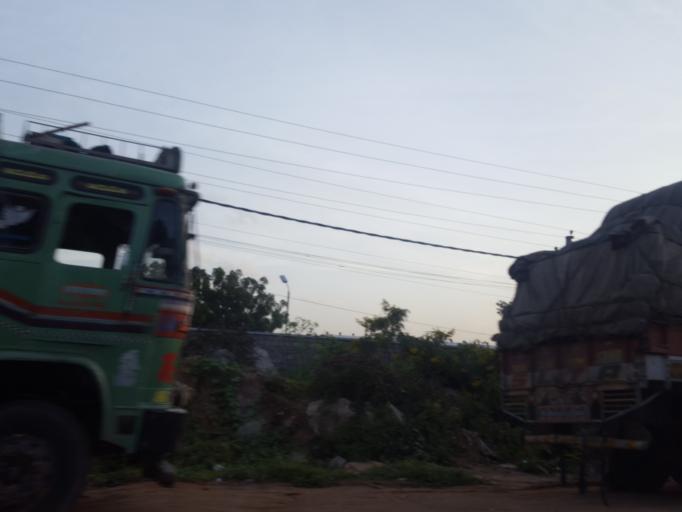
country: IN
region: Telangana
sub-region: Rangareddi
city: Kukatpalli
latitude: 17.5408
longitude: 78.3932
